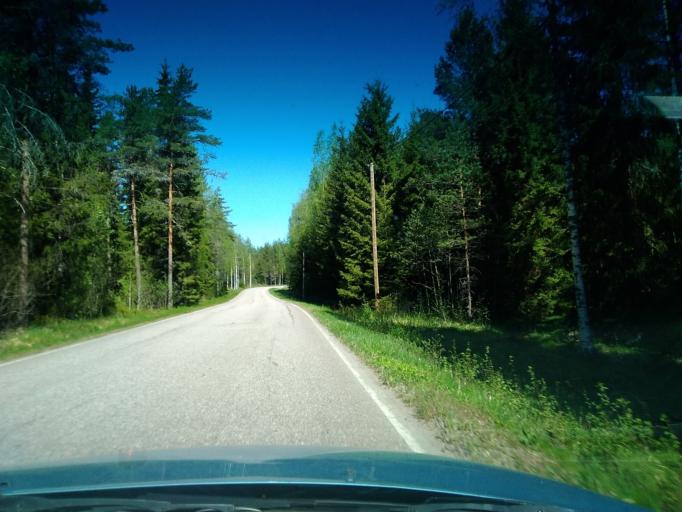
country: FI
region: Uusimaa
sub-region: Helsinki
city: Kaerkoelae
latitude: 60.6400
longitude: 23.9279
